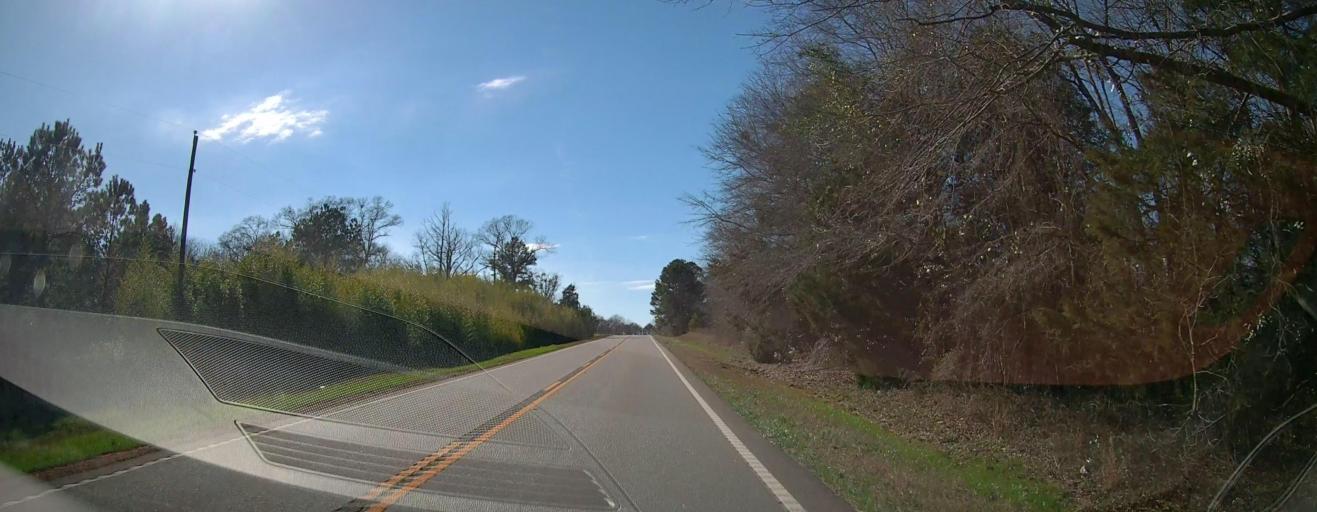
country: US
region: Georgia
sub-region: Macon County
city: Oglethorpe
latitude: 32.3516
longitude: -84.1633
